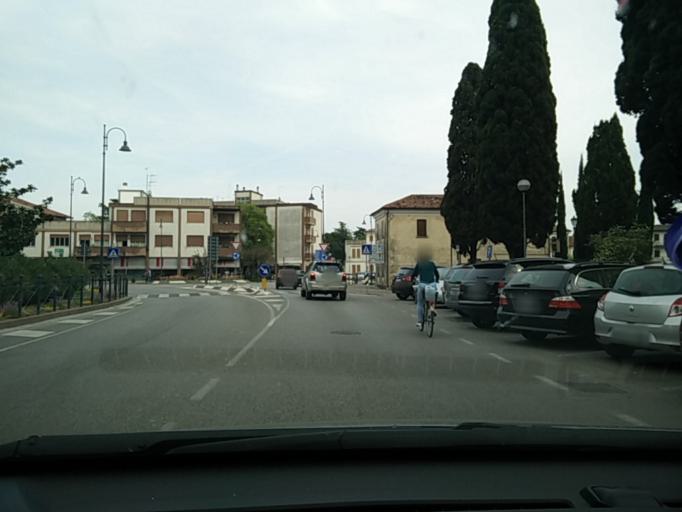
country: IT
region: Veneto
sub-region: Provincia di Venezia
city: Noventa di Piave
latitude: 45.6624
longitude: 12.5291
